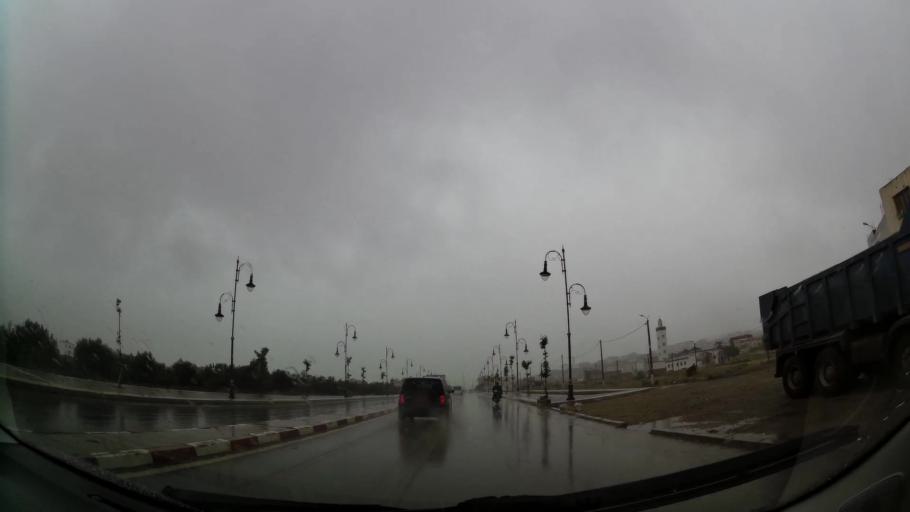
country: MA
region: Taza-Al Hoceima-Taounate
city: Imzourene
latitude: 35.1389
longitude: -3.8476
